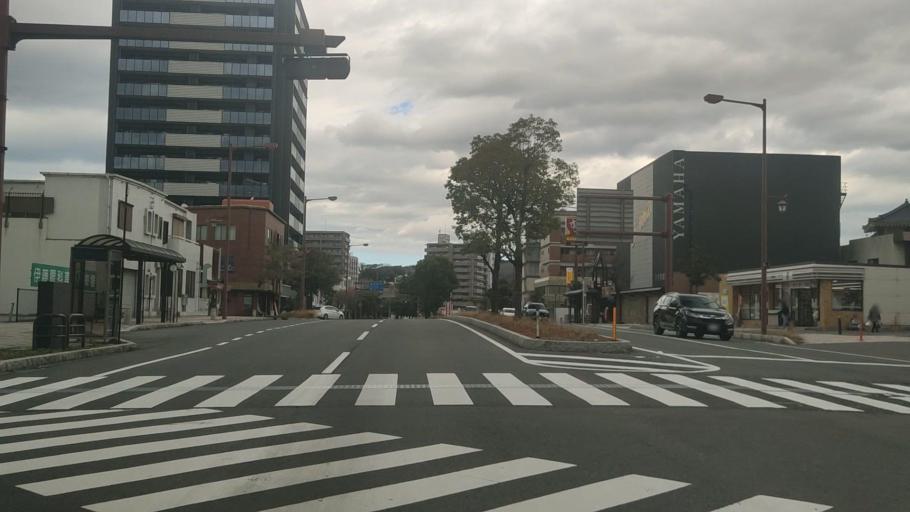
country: JP
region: Yamaguchi
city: Shimonoseki
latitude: 33.9587
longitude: 130.9422
